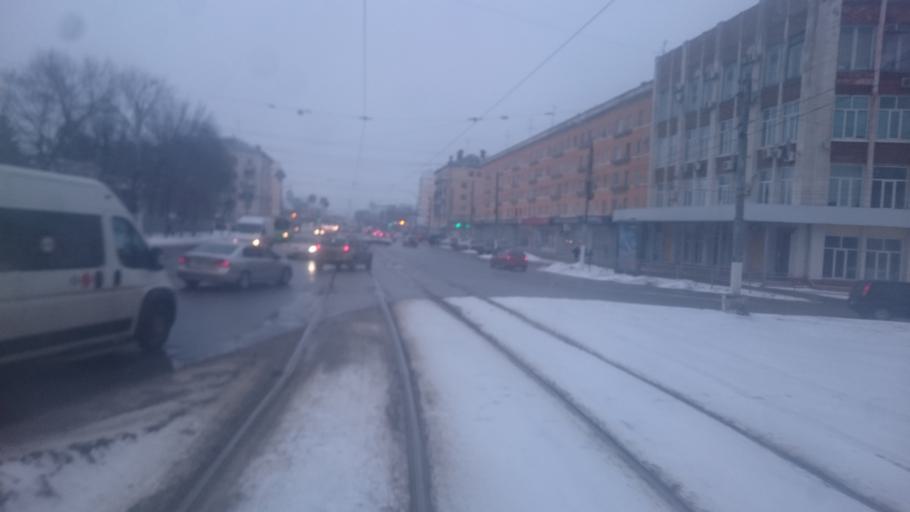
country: RU
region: Tverskaya
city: Tver
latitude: 56.8461
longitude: 35.9050
